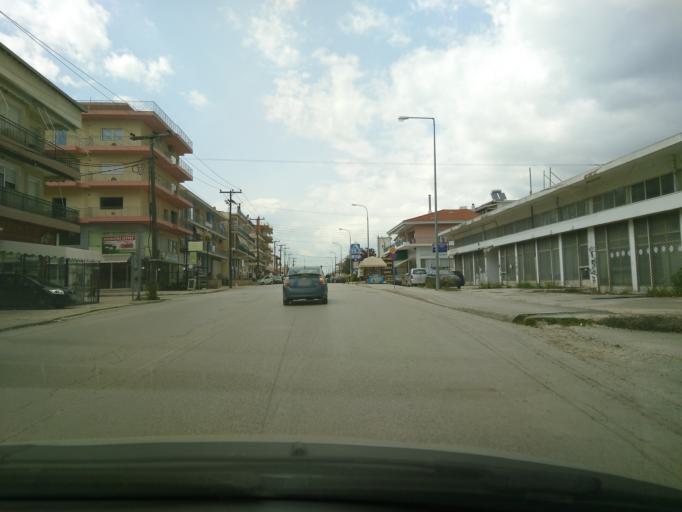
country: GR
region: Epirus
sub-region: Nomos Ioanninon
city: Eksochi
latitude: 39.6824
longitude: 20.8358
